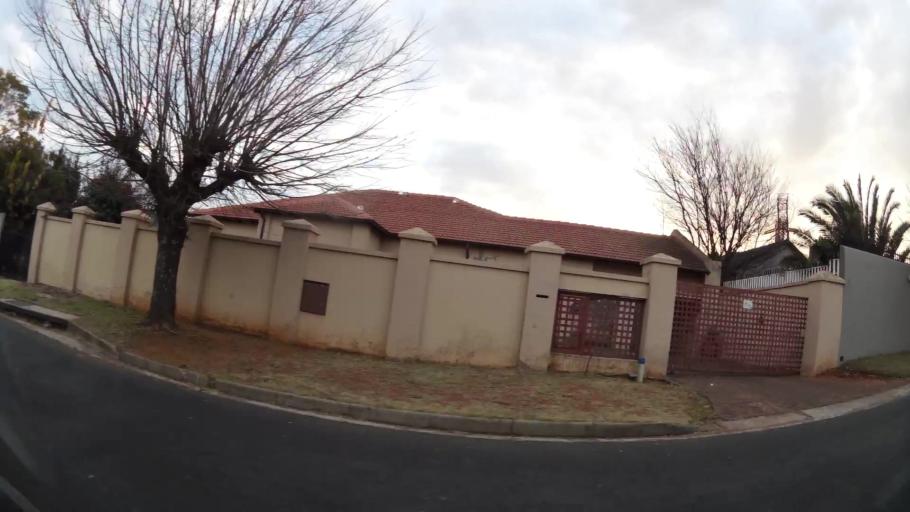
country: ZA
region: Gauteng
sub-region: Ekurhuleni Metropolitan Municipality
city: Germiston
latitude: -26.1927
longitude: 28.1470
